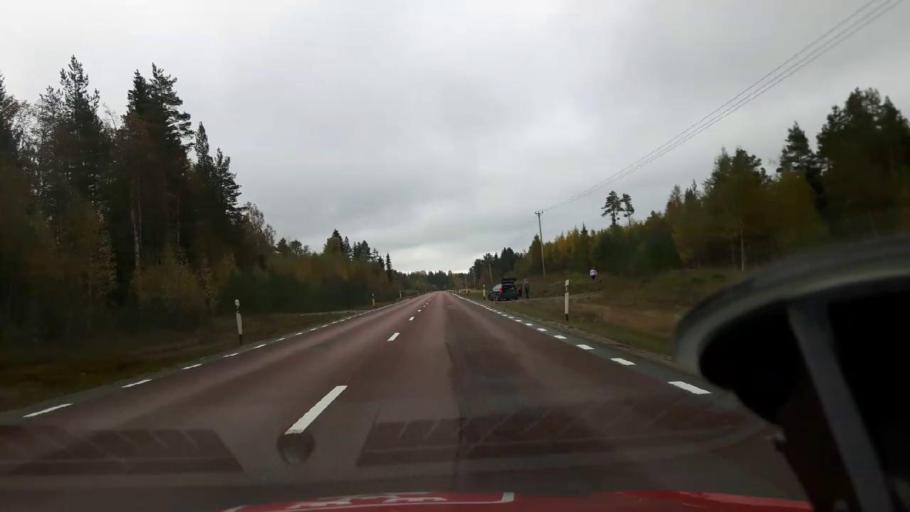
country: SE
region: Jaemtland
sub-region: Harjedalens Kommun
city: Sveg
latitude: 62.2655
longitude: 14.8089
